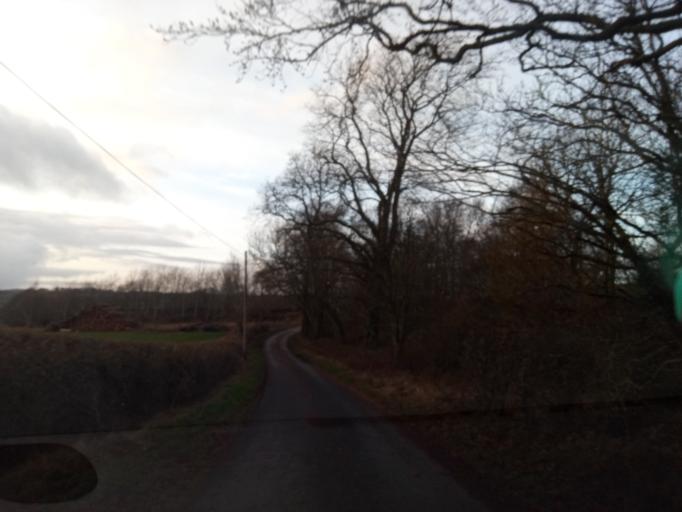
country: GB
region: Scotland
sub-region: The Scottish Borders
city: Newtown St Boswells
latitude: 55.5357
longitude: -2.7132
